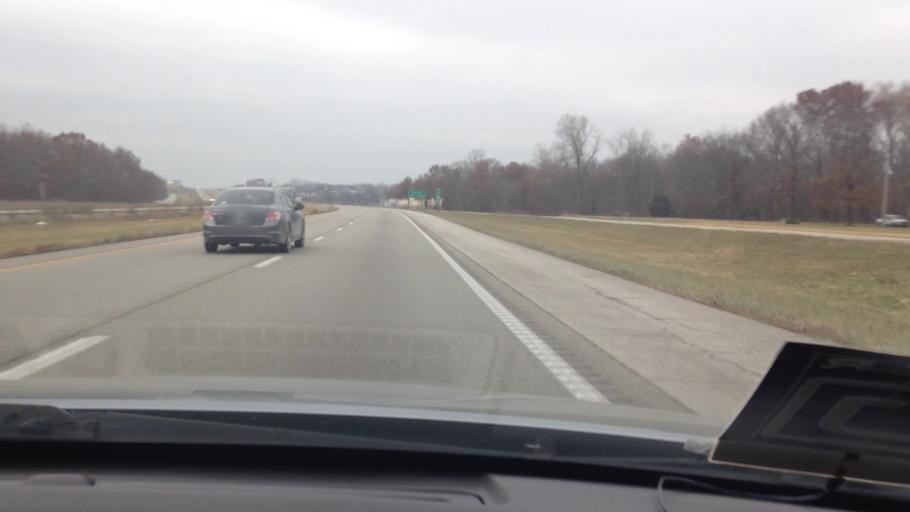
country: US
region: Missouri
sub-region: Cass County
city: Peculiar
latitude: 38.6955
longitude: -94.4298
